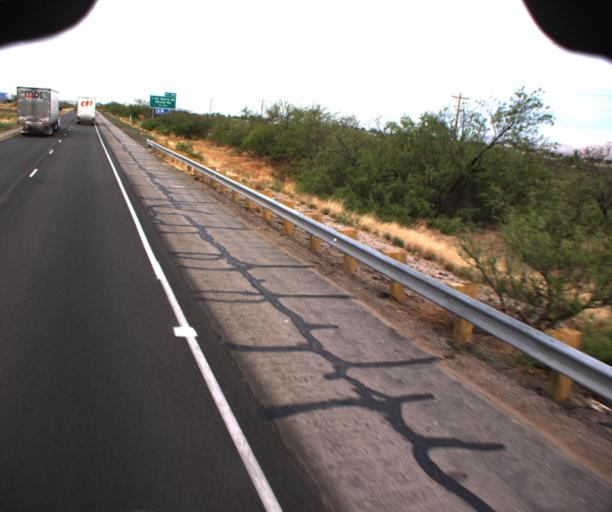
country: US
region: Arizona
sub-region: Cochise County
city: Mescal
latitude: 31.9632
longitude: -110.4192
